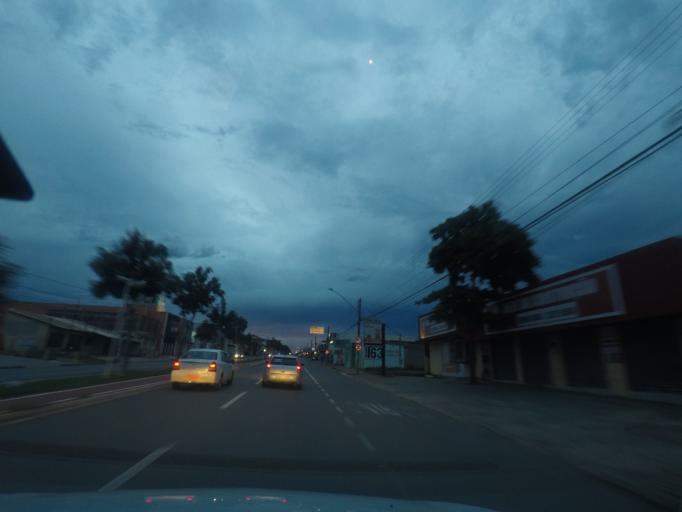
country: BR
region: Goias
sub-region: Goiania
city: Goiania
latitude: -16.7187
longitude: -49.2971
